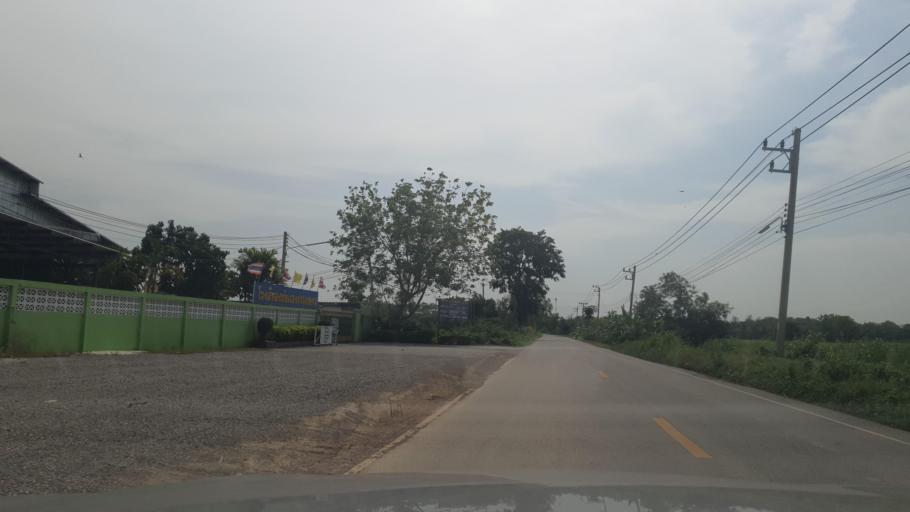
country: TH
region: Sukhothai
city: Si Samrong
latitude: 17.1201
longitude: 99.8607
